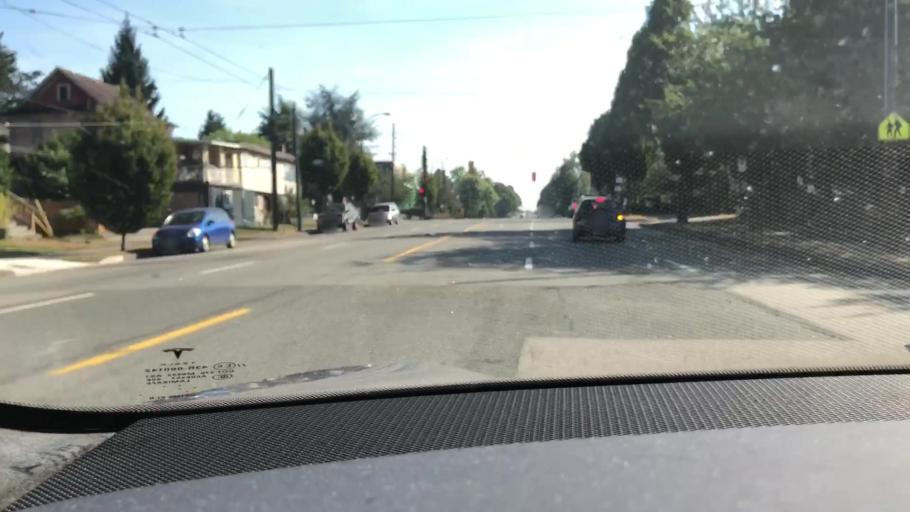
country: CA
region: British Columbia
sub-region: Fraser Valley Regional District
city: North Vancouver
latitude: 49.2876
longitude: -123.0566
